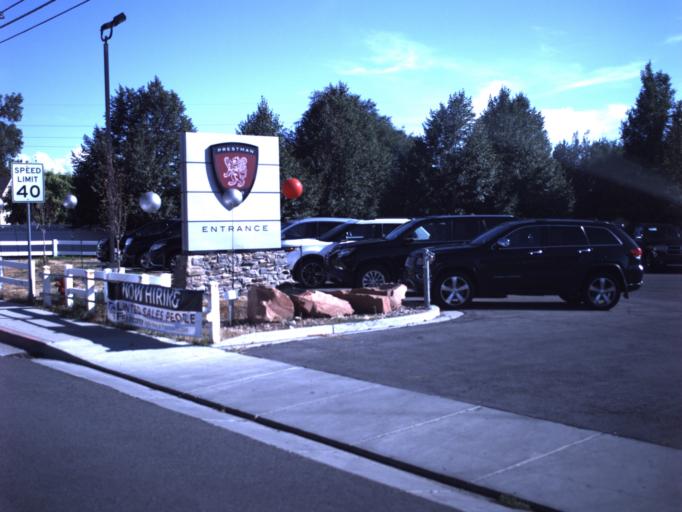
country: US
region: Utah
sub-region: Utah County
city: Lindon
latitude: 40.3387
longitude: -111.7177
